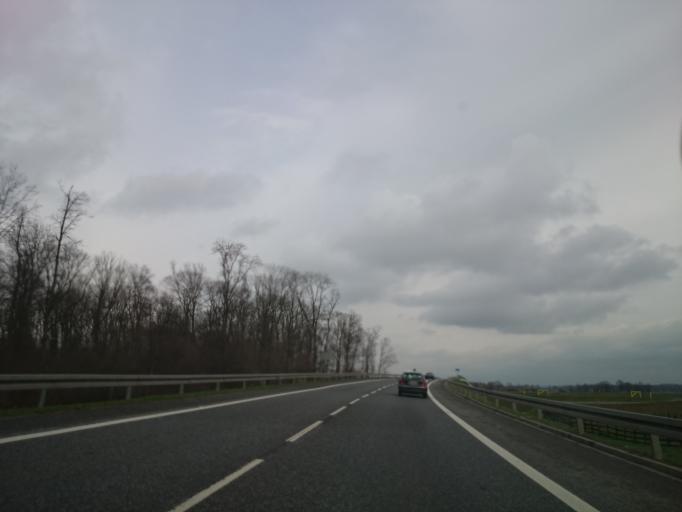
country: PL
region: Opole Voivodeship
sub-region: Powiat nyski
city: Otmuchow
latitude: 50.4583
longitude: 17.1717
